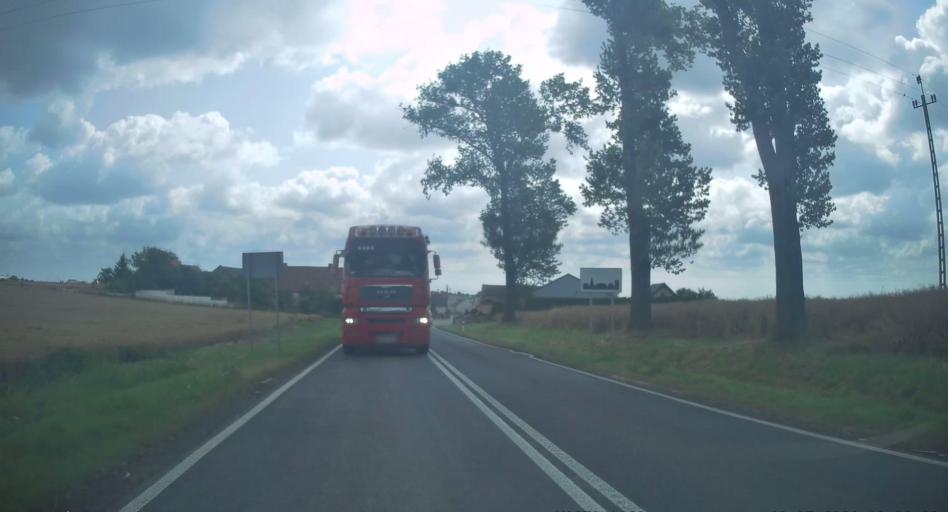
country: PL
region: Opole Voivodeship
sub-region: Powiat prudnicki
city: Glogowek
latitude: 50.3373
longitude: 17.9264
